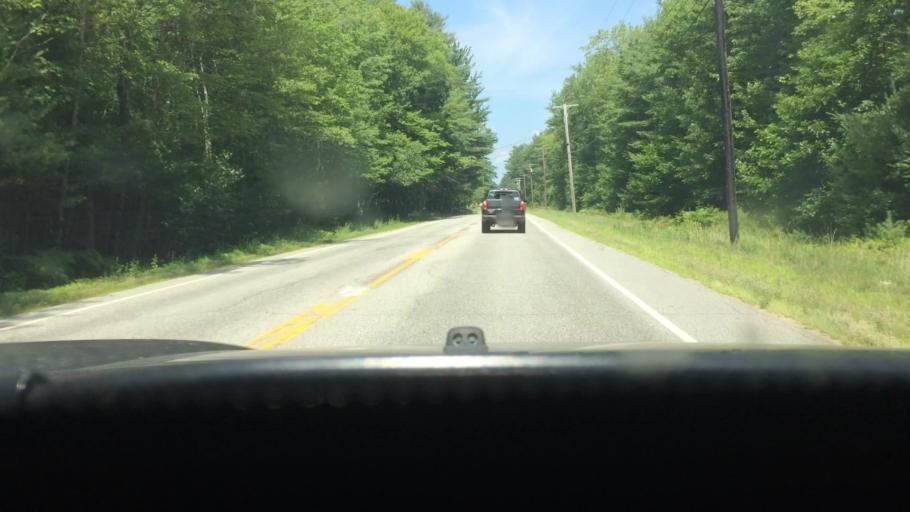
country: US
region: Maine
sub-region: Androscoggin County
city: Mechanic Falls
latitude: 44.0981
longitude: -70.3595
